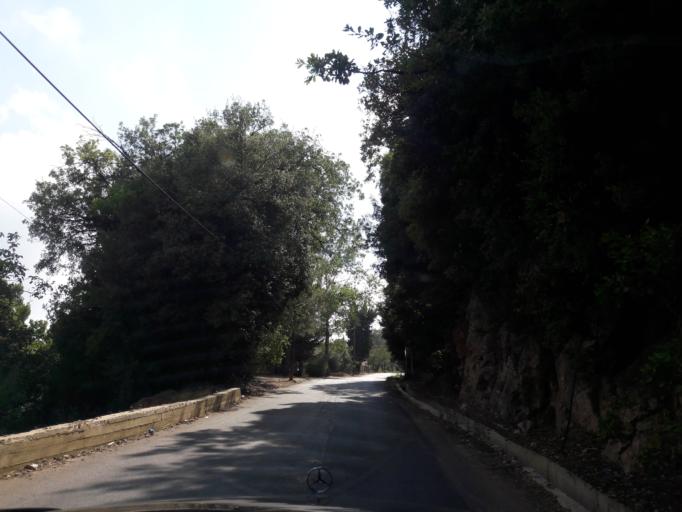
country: LB
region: Mont-Liban
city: Djounie
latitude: 33.9637
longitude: 35.7775
